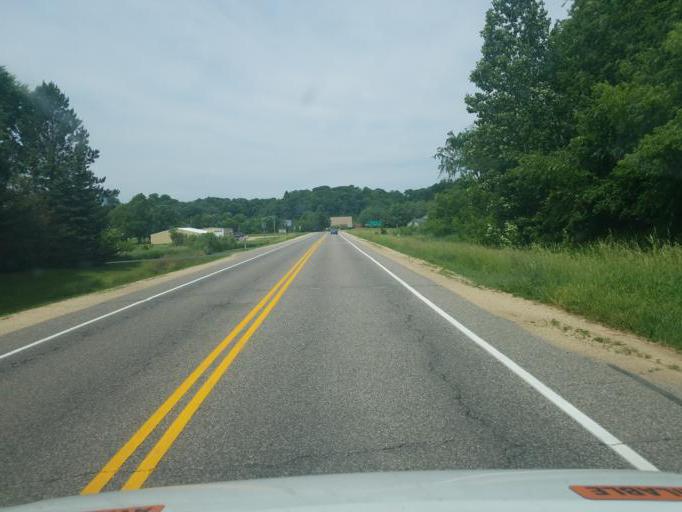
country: US
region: Wisconsin
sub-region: Juneau County
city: Elroy
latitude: 43.7605
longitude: -90.2688
